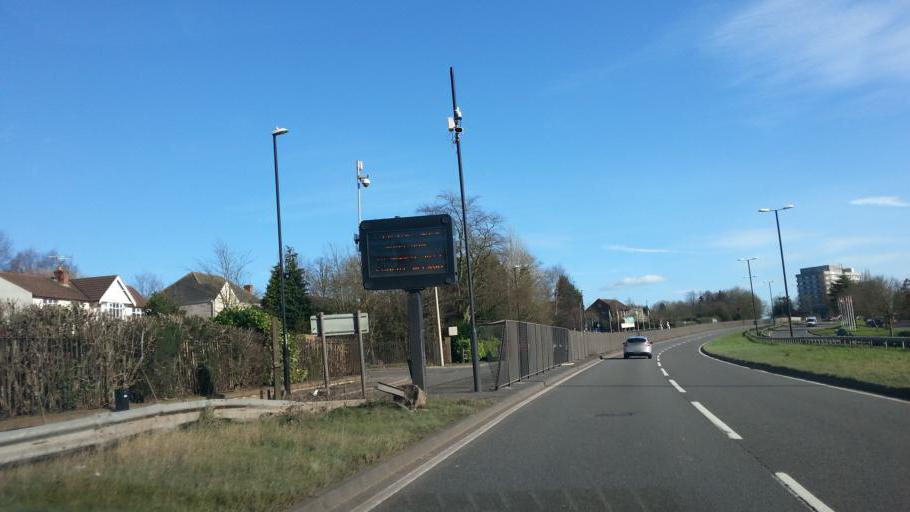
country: GB
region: England
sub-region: Coventry
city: Keresley
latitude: 52.4281
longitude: -1.5784
